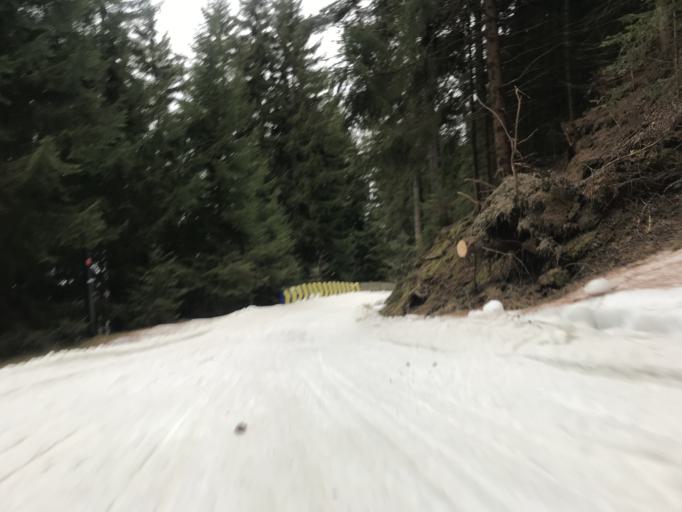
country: IT
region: Trentino-Alto Adige
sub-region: Bolzano
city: Bressanone
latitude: 46.6930
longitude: 11.6874
